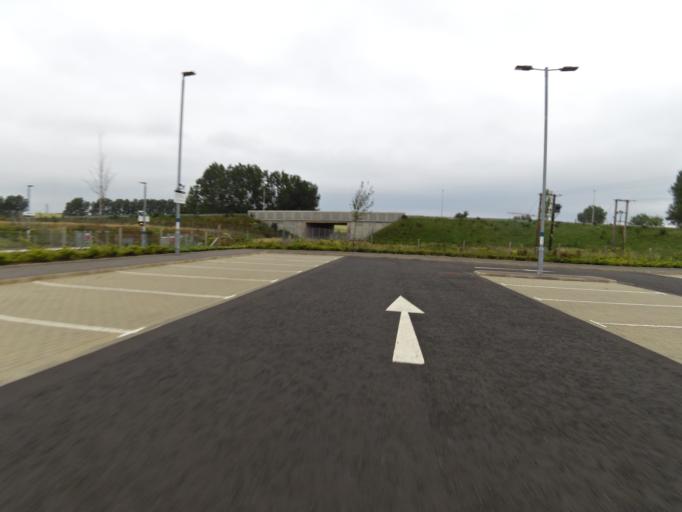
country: GB
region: Scotland
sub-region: Midlothian
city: Dalkeith
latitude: 55.9180
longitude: -3.0898
